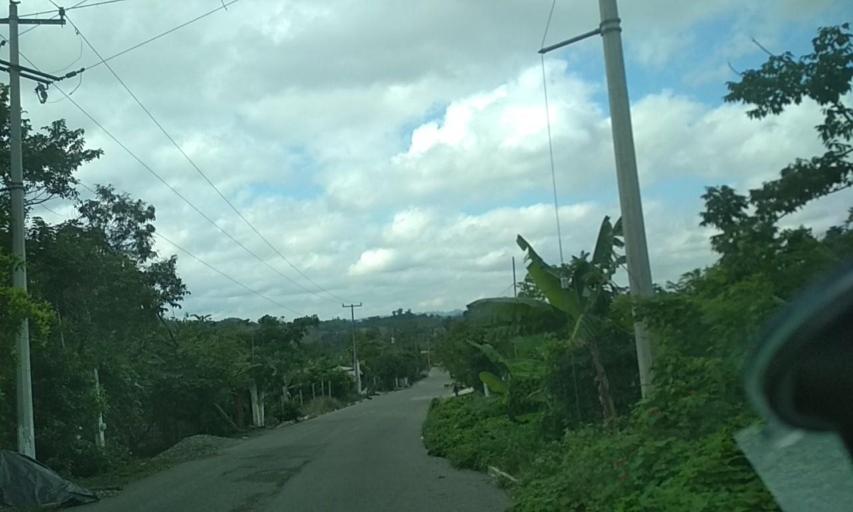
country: MX
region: Veracruz
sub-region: Papantla
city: Polutla
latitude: 20.5407
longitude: -97.2472
